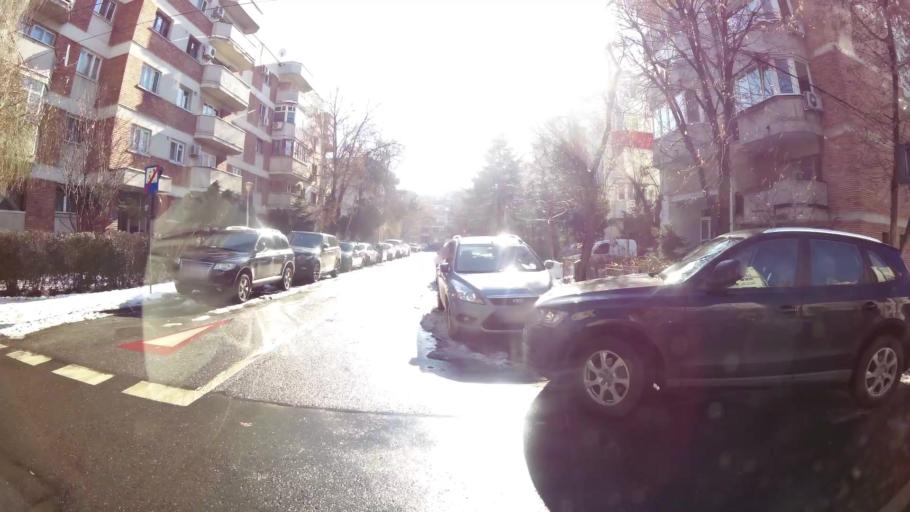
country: RO
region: Bucuresti
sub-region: Municipiul Bucuresti
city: Bucharest
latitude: 44.4627
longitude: 26.0968
